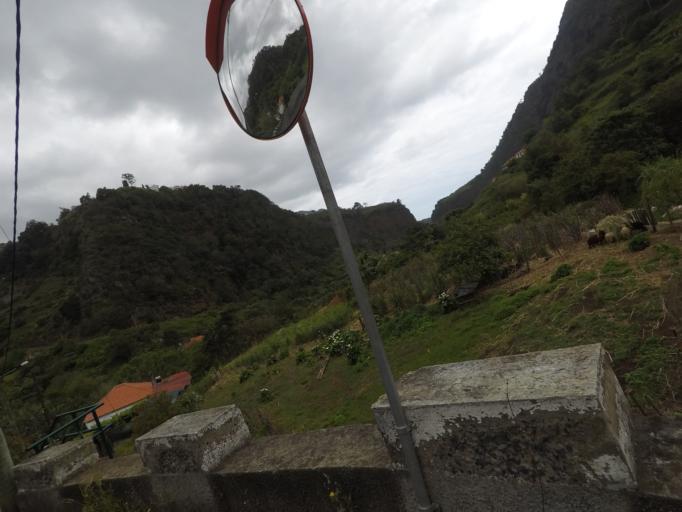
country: PT
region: Madeira
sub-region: Santana
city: Santana
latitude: 32.7737
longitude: -16.8470
